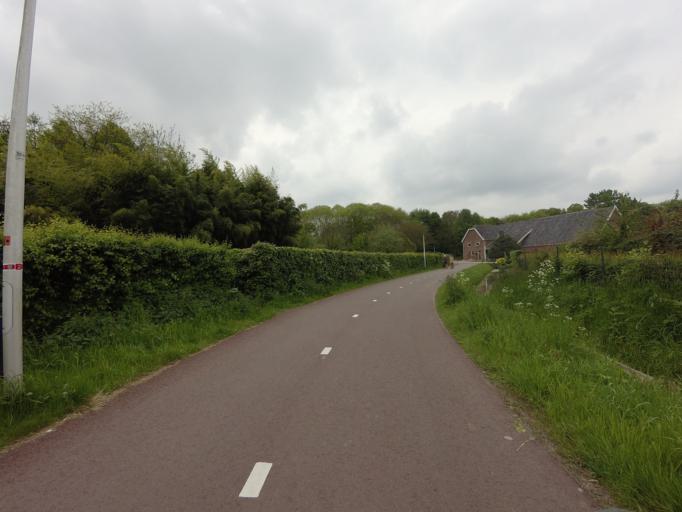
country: NL
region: Utrecht
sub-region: Gemeente Houten
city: Houten
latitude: 52.0406
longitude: 5.1581
